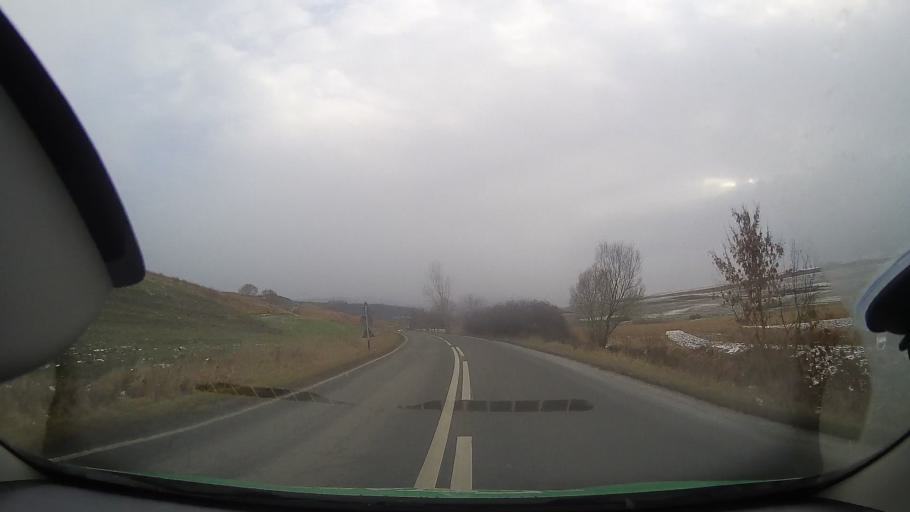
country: RO
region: Sibiu
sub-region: Comuna Blajel
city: Blajel
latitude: 46.2347
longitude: 24.3090
